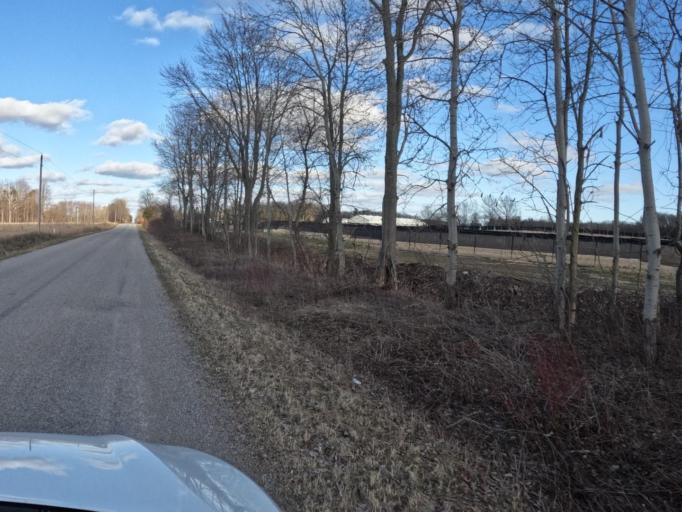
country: CA
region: Ontario
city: Norfolk County
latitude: 42.8154
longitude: -80.5692
